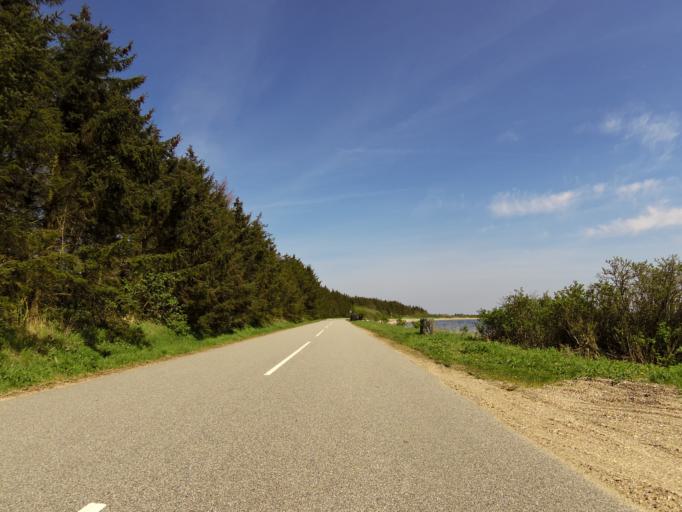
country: DK
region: Central Jutland
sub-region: Struer Kommune
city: Struer
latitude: 56.5175
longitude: 8.6000
